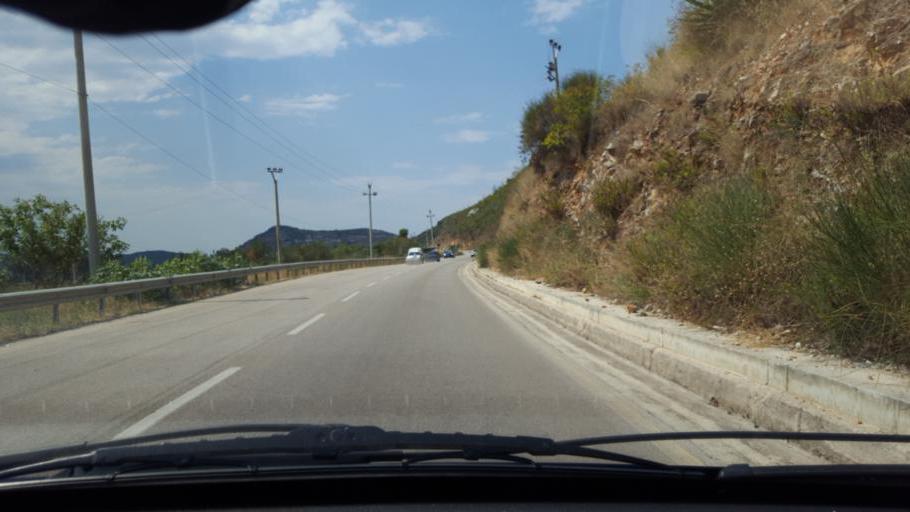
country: AL
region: Vlore
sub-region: Rrethi i Sarandes
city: Sarande
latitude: 39.8226
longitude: 20.0205
